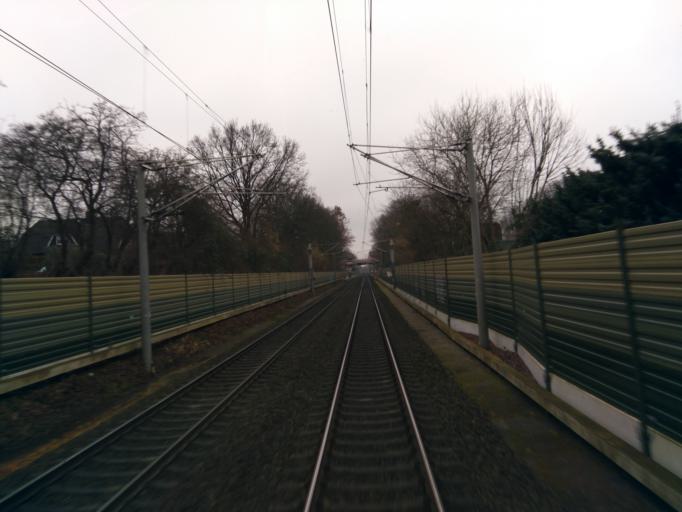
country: DE
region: Hamburg
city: Harburg
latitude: 53.4244
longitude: 10.0176
